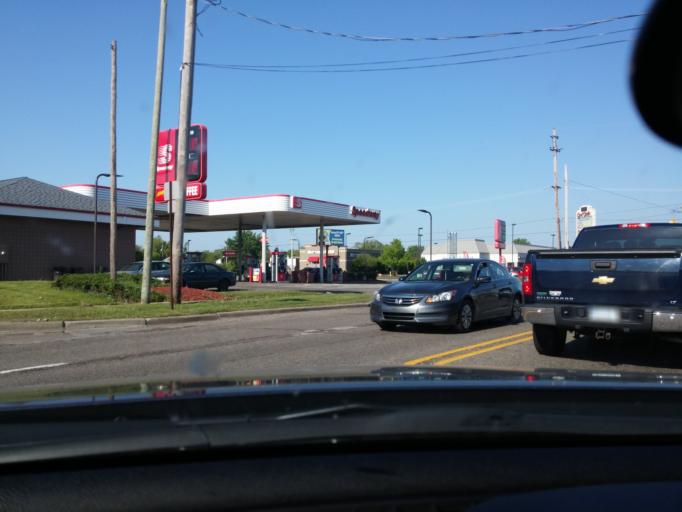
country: US
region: Michigan
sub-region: Genesee County
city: Burton
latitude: 43.0188
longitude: -83.6340
